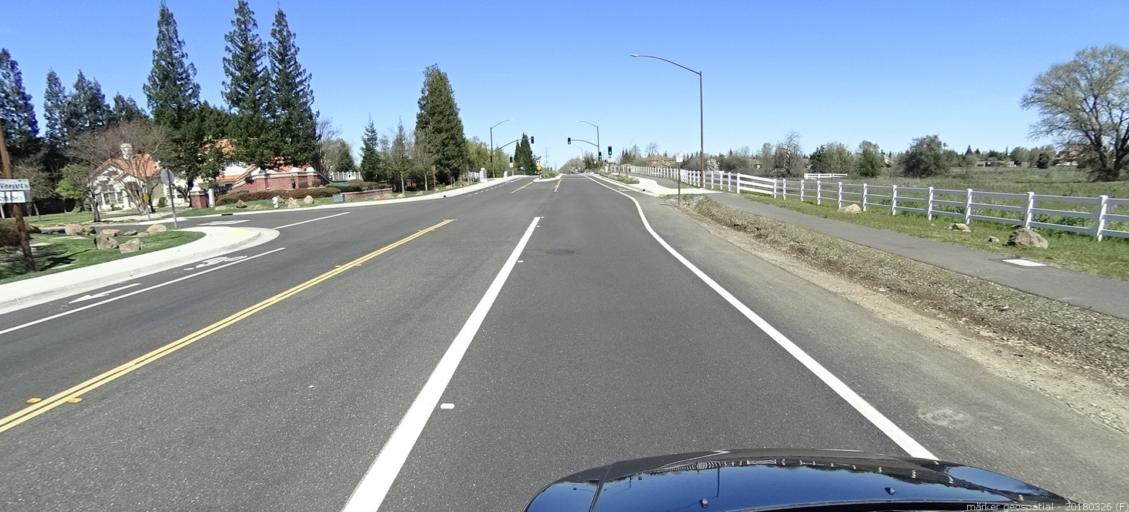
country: US
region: California
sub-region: Sacramento County
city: Vineyard
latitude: 38.4625
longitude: -121.3160
